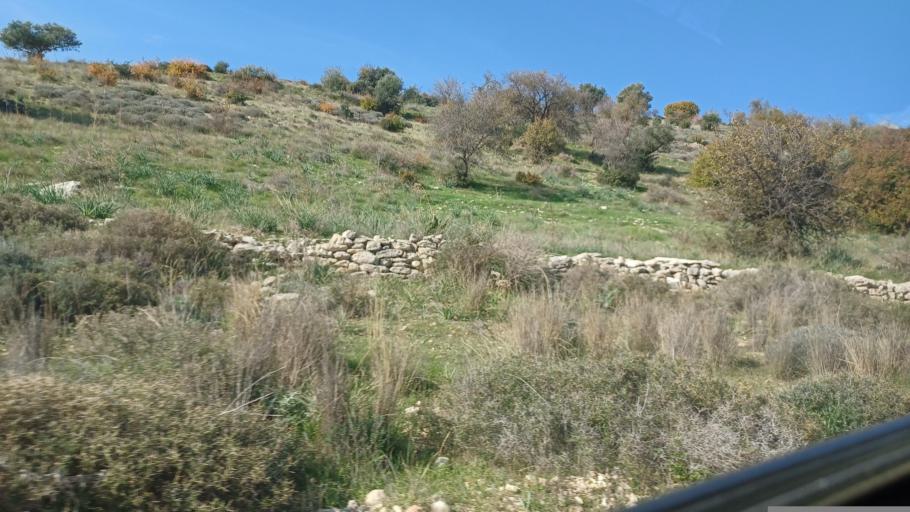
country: CY
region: Pafos
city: Mesogi
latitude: 34.7611
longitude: 32.5639
